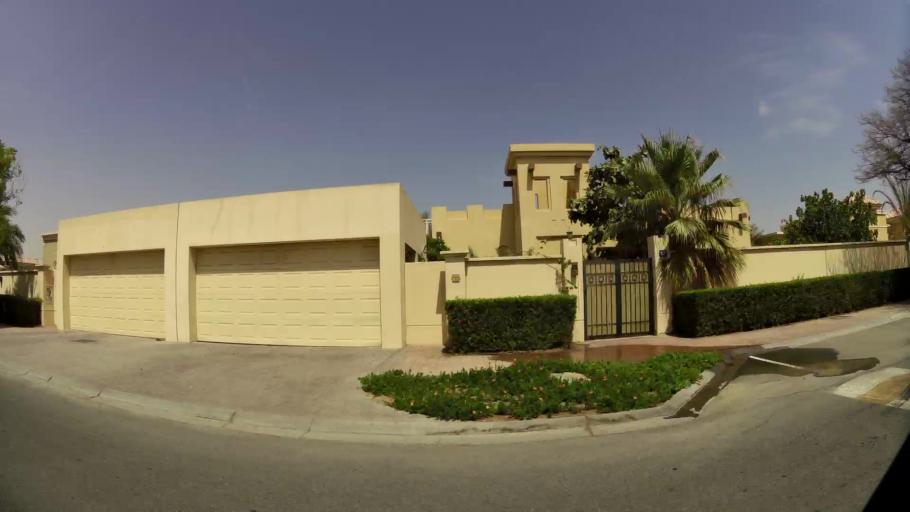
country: AE
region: Ash Shariqah
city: Sharjah
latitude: 25.1844
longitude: 55.4438
